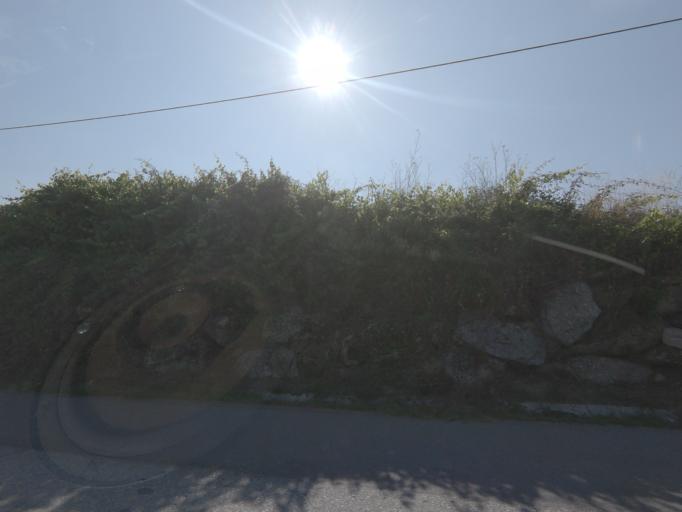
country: PT
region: Viseu
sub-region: Moimenta da Beira
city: Moimenta da Beira
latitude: 40.9887
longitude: -7.5626
